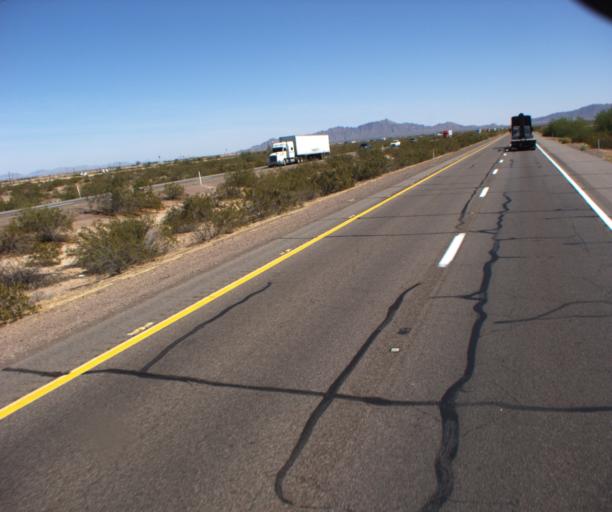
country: US
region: Arizona
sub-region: Yuma County
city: Wellton
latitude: 32.6992
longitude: -113.9147
